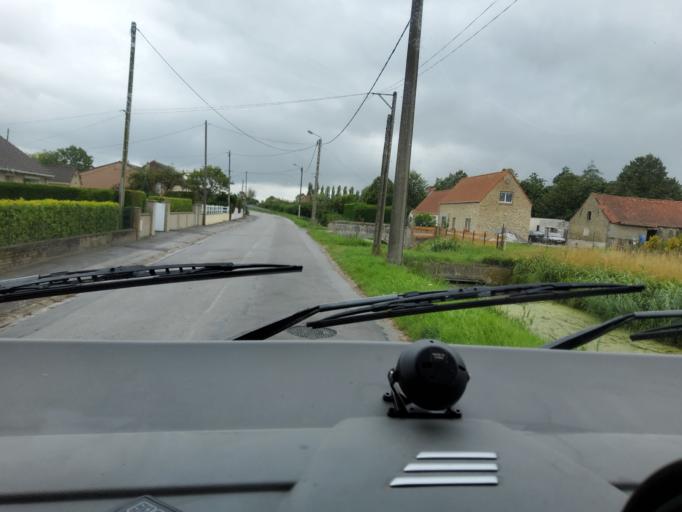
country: FR
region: Nord-Pas-de-Calais
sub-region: Departement du Pas-de-Calais
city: Saint-Folquin
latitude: 50.9501
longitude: 2.1282
